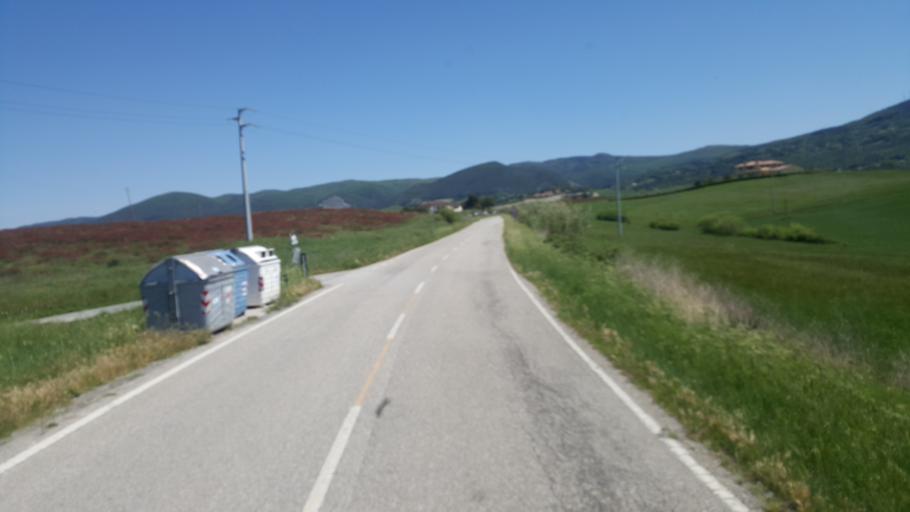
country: IT
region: Tuscany
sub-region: Province of Pisa
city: Castellina Marittima
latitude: 43.4243
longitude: 10.5297
